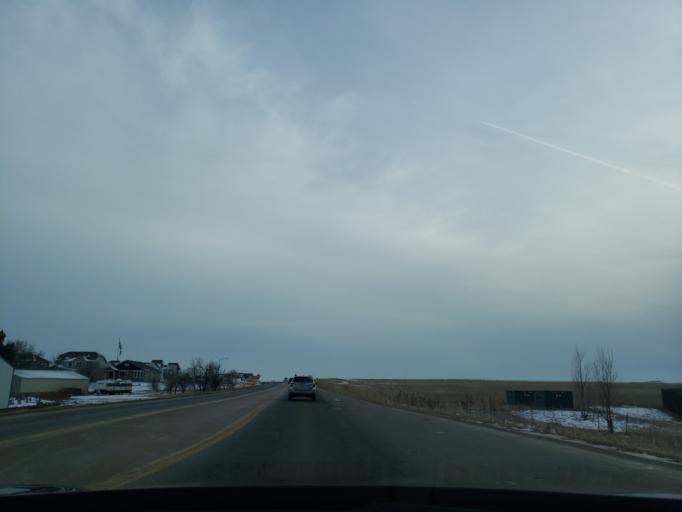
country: US
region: Colorado
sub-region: Larimer County
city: Campion
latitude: 40.3431
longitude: -105.0936
